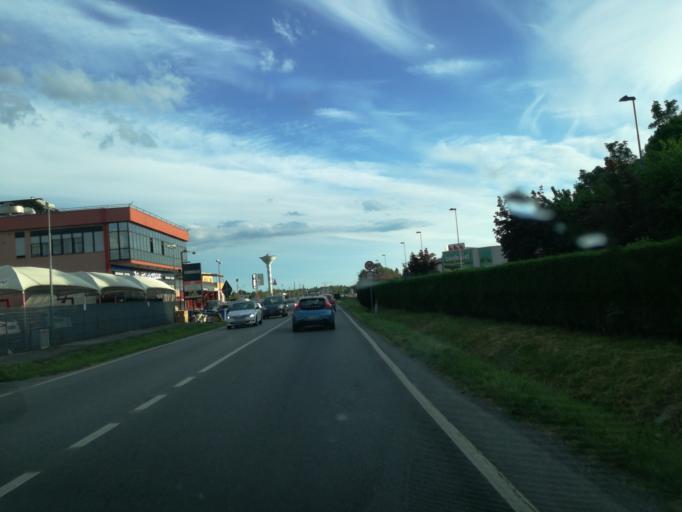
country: IT
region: Lombardy
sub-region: Provincia di Lecco
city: Osnago
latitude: 45.6783
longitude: 9.3965
